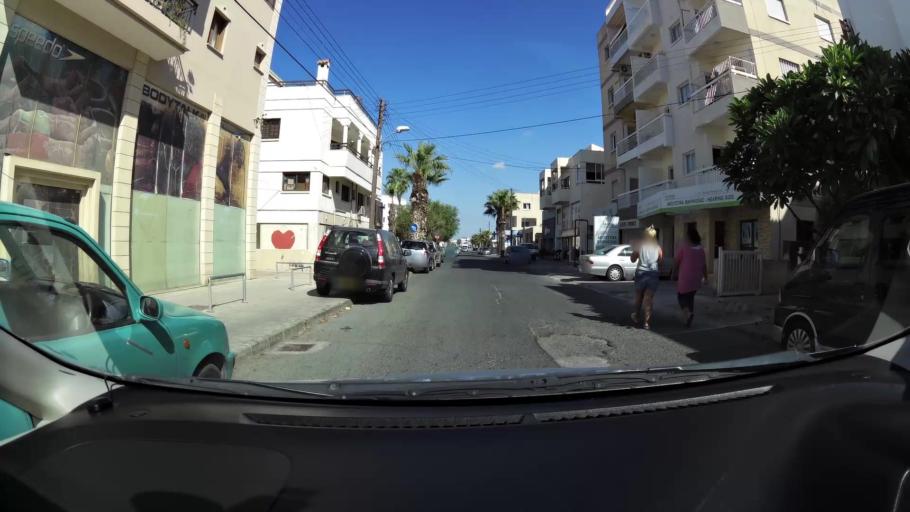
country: CY
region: Larnaka
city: Larnaca
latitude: 34.9258
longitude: 33.6338
